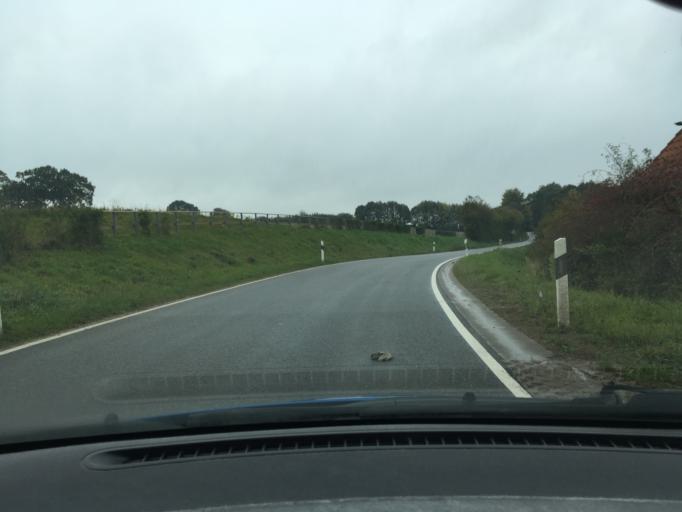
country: DE
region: Schleswig-Holstein
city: Nehmten
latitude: 54.0784
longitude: 10.3989
